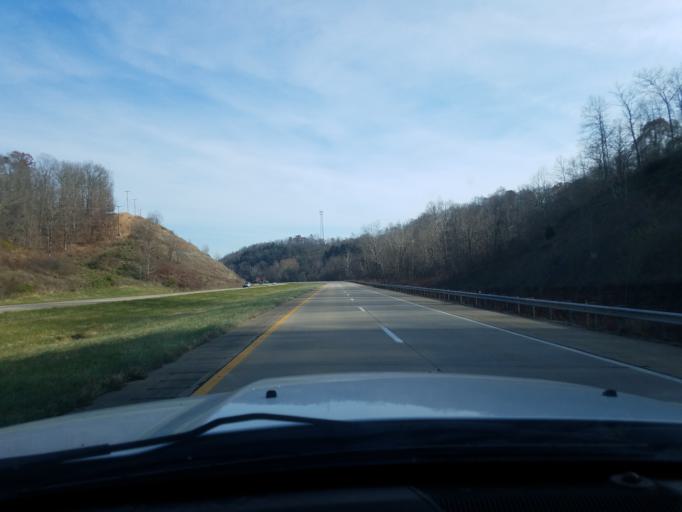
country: US
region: West Virginia
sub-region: Wood County
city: Washington
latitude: 39.2150
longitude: -81.8519
